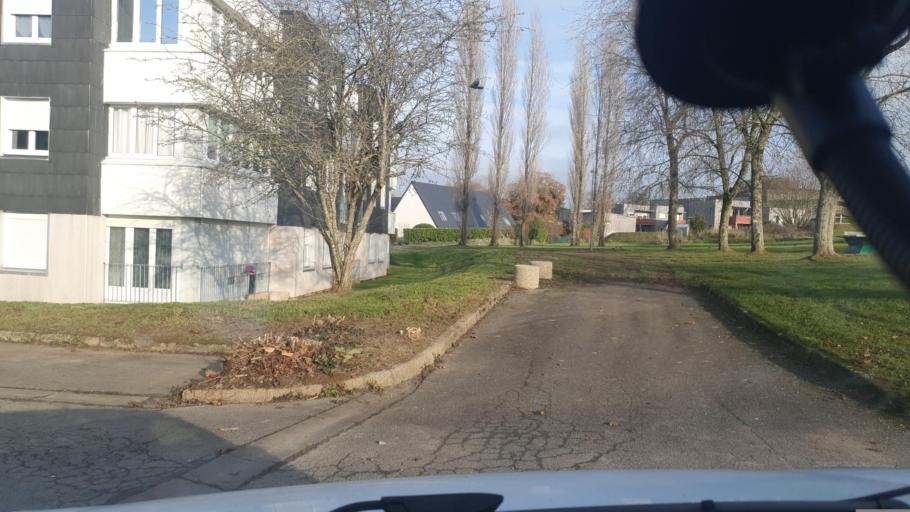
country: FR
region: Brittany
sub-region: Departement du Finistere
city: Briec
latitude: 48.1050
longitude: -4.0071
